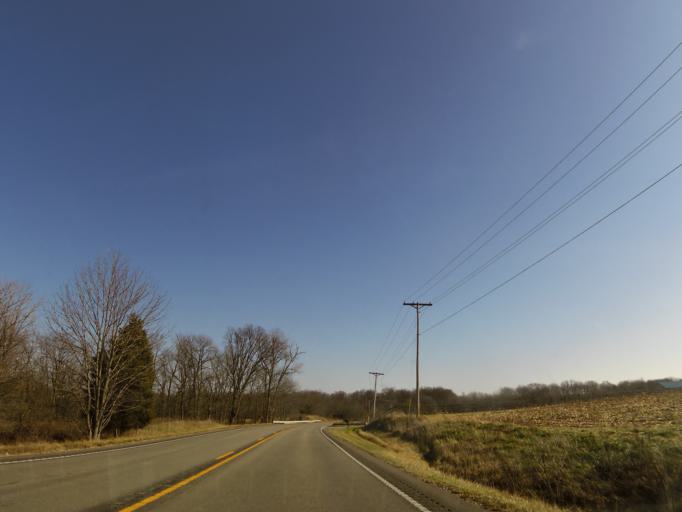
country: US
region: Indiana
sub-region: Union County
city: Liberty
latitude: 39.6349
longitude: -85.0346
